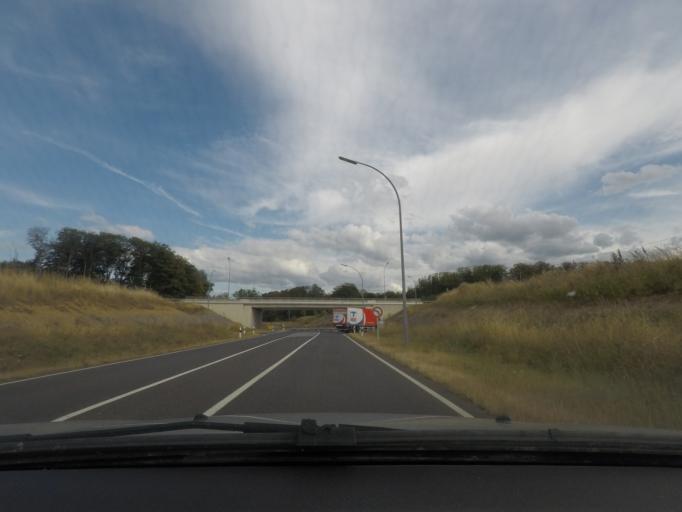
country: LU
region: Grevenmacher
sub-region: Canton d'Echternach
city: Consdorf
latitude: 49.7580
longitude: 6.3398
